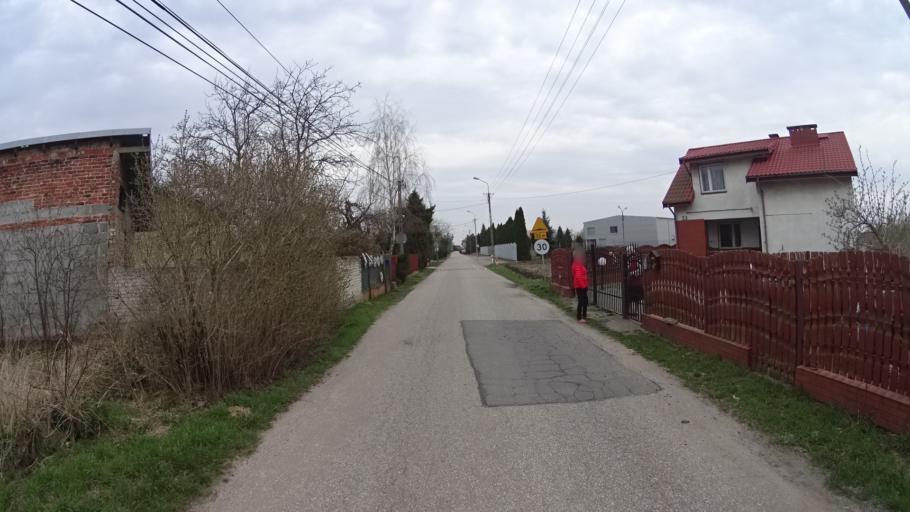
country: PL
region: Masovian Voivodeship
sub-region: Powiat warszawski zachodni
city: Jozefow
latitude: 52.2075
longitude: 20.6659
